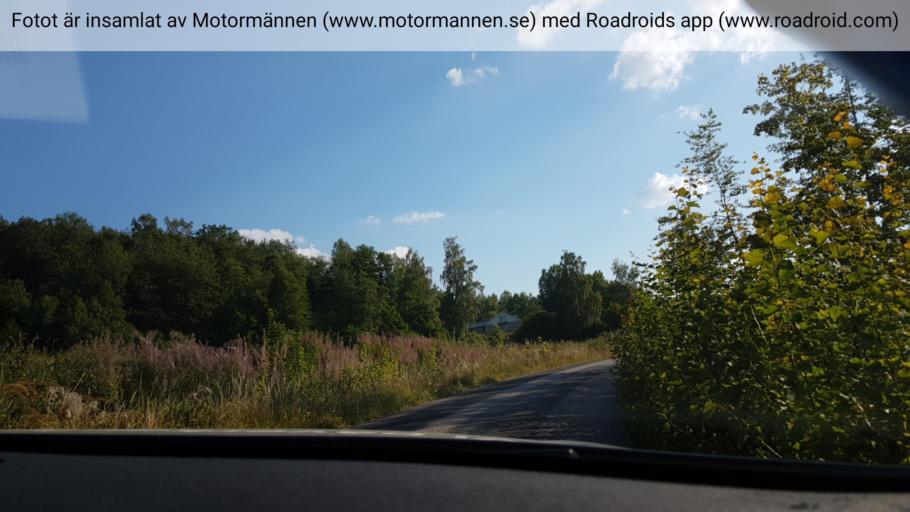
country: SE
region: Vaestra Goetaland
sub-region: Skovde Kommun
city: Skoevde
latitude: 58.4464
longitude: 13.7082
